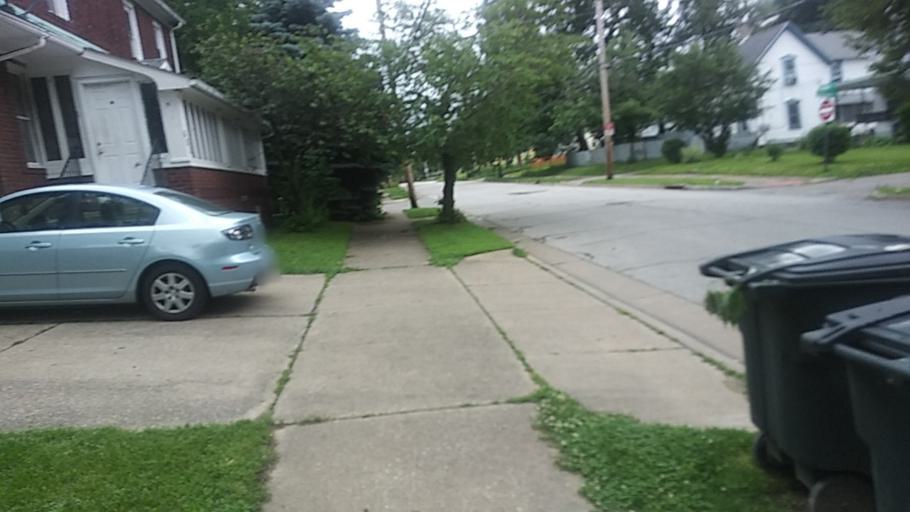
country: US
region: Ohio
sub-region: Summit County
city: Akron
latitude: 41.0802
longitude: -81.4952
